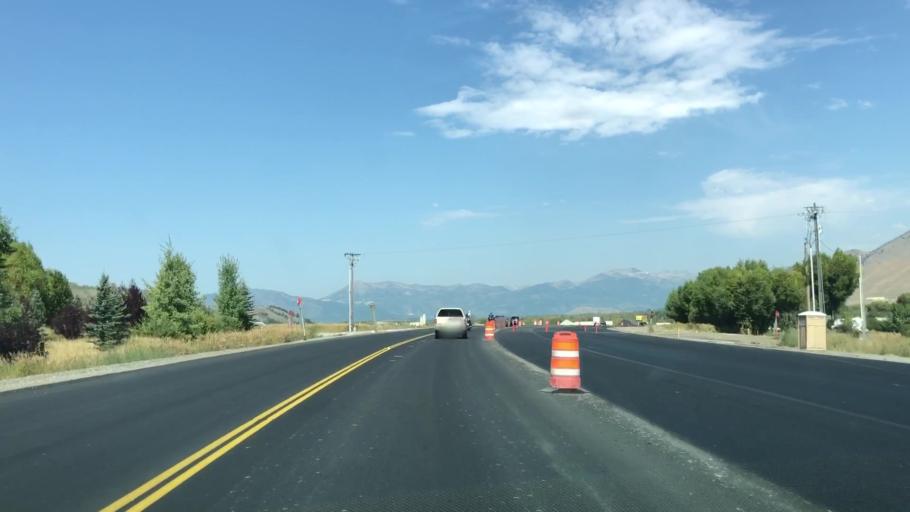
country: US
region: Wyoming
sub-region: Teton County
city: South Park
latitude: 43.3723
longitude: -110.7427
